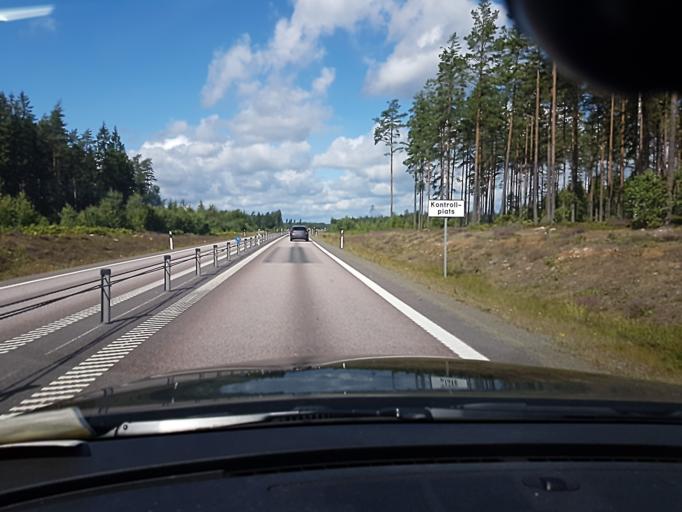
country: SE
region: Kalmar
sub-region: Emmaboda Kommun
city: Emmaboda
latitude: 56.7263
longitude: 15.5689
